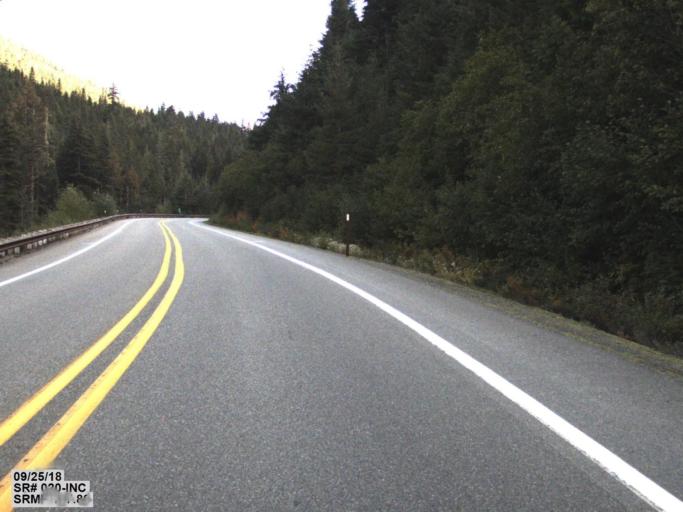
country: US
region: Washington
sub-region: Snohomish County
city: Darrington
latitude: 48.6298
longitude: -120.8448
